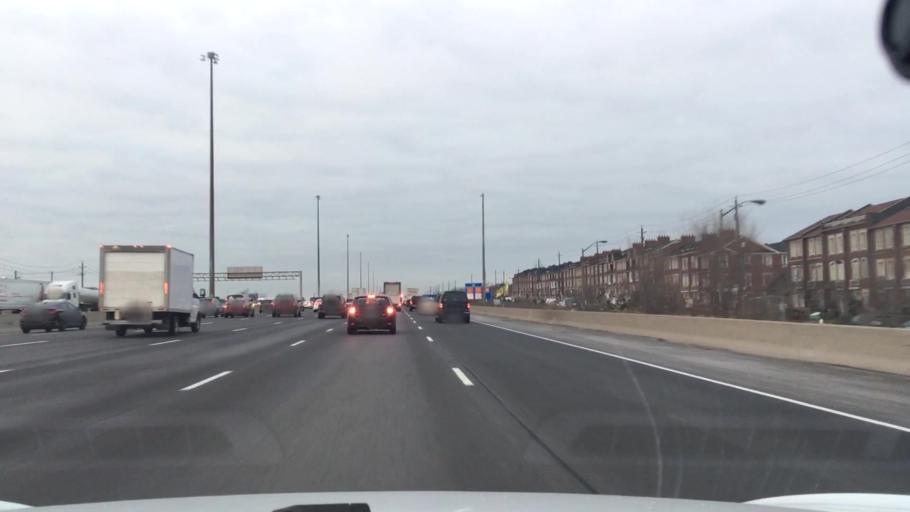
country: CA
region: Ontario
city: Concord
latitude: 43.7266
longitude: -79.5236
